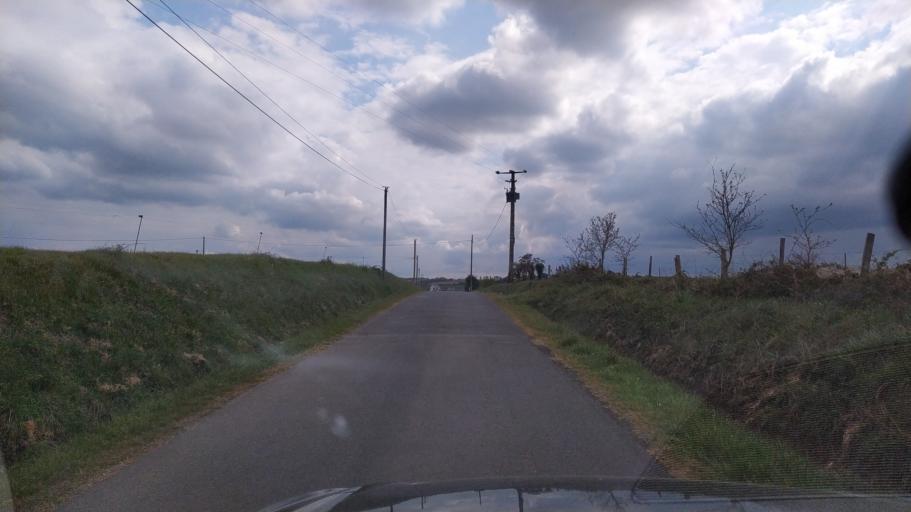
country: FR
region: Brittany
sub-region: Departement du Finistere
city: Bodilis
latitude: 48.5095
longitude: -4.1175
